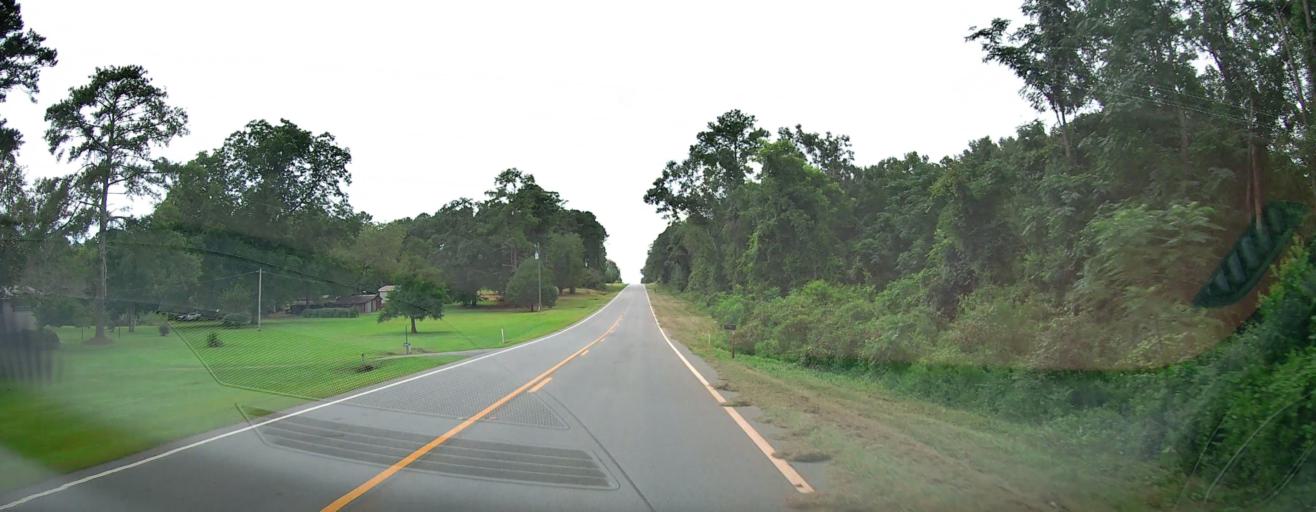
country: US
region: Georgia
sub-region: Macon County
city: Oglethorpe
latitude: 32.2759
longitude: -84.1301
